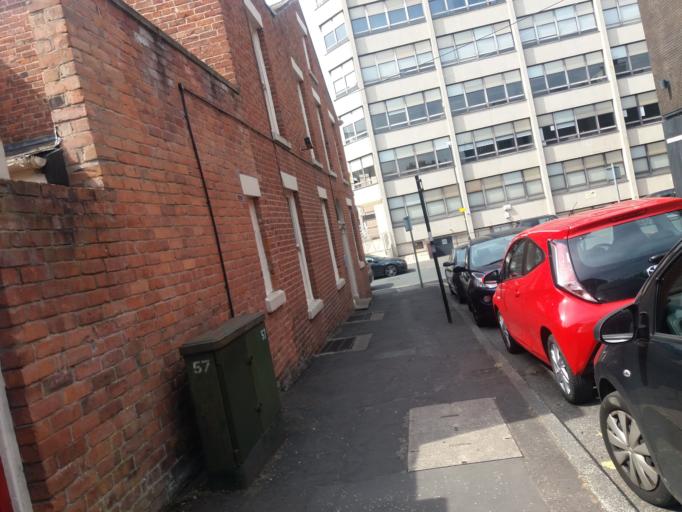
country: GB
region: England
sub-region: Lancashire
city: Preston
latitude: 53.7562
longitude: -2.6994
